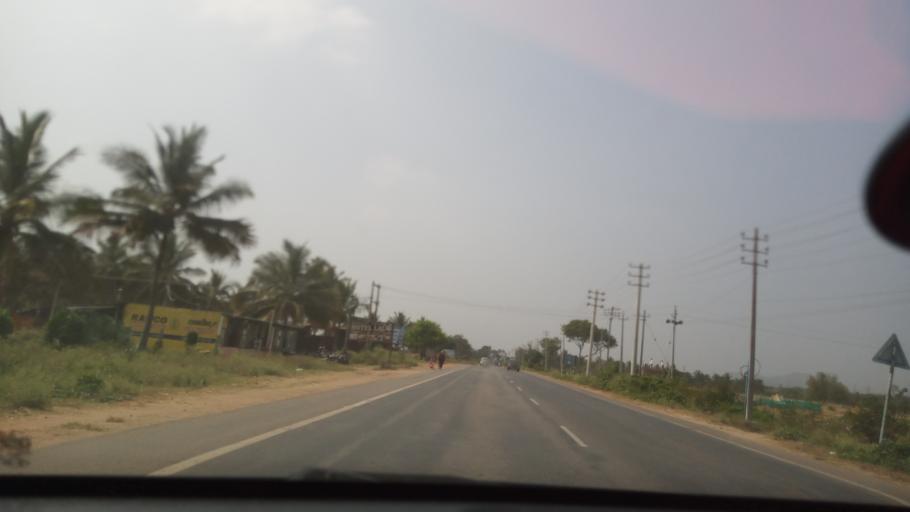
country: IN
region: Karnataka
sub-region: Chamrajnagar
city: Chamrajnagar
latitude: 11.9911
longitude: 76.8650
